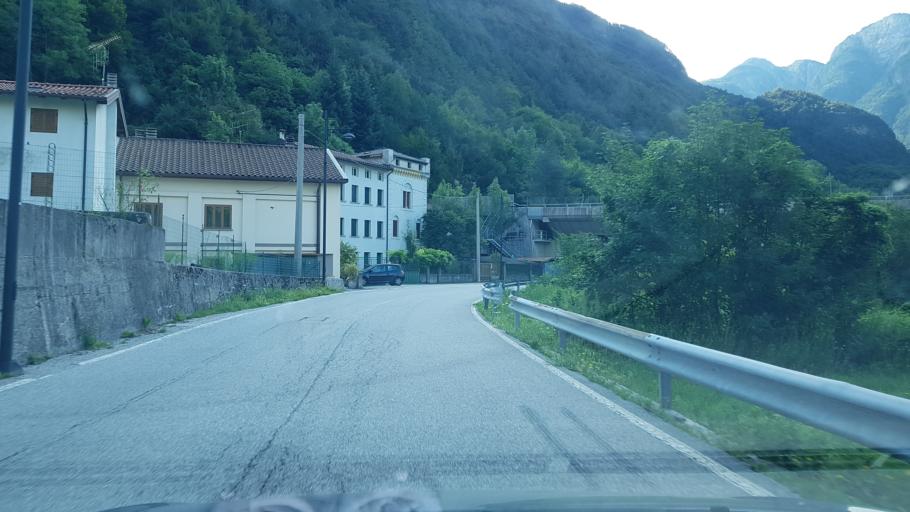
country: IT
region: Friuli Venezia Giulia
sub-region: Provincia di Udine
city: Chiusaforte
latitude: 46.4077
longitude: 13.3147
